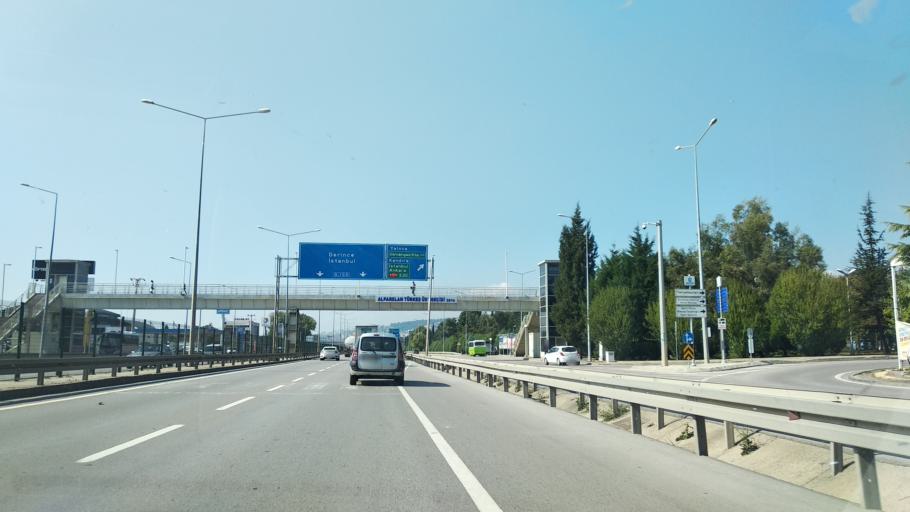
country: TR
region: Kocaeli
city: Kullar
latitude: 40.7603
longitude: 29.9761
